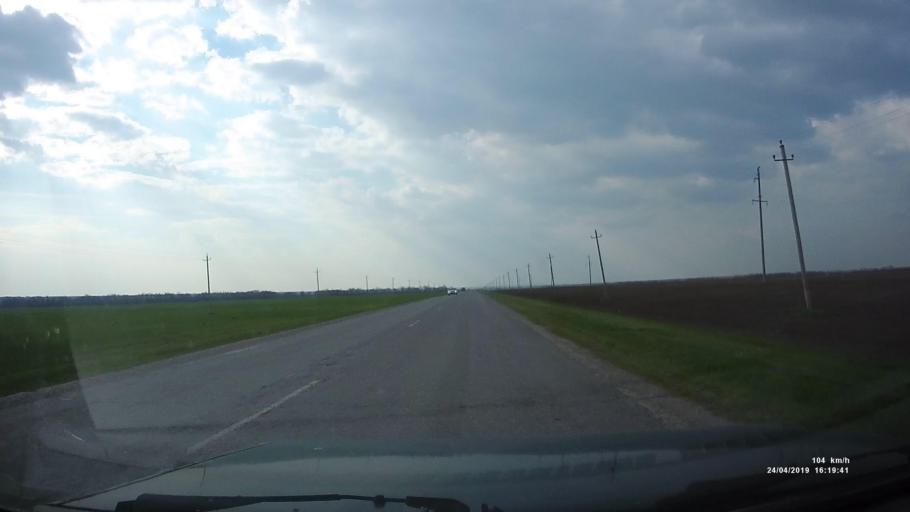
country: RU
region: Rostov
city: Sovetskoye
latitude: 46.7845
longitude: 42.0919
